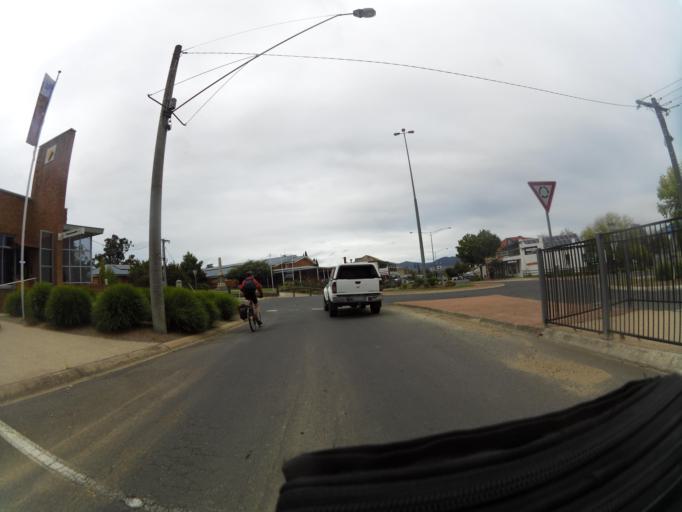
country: AU
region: New South Wales
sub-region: Snowy River
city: Jindabyne
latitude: -36.1947
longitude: 147.9073
